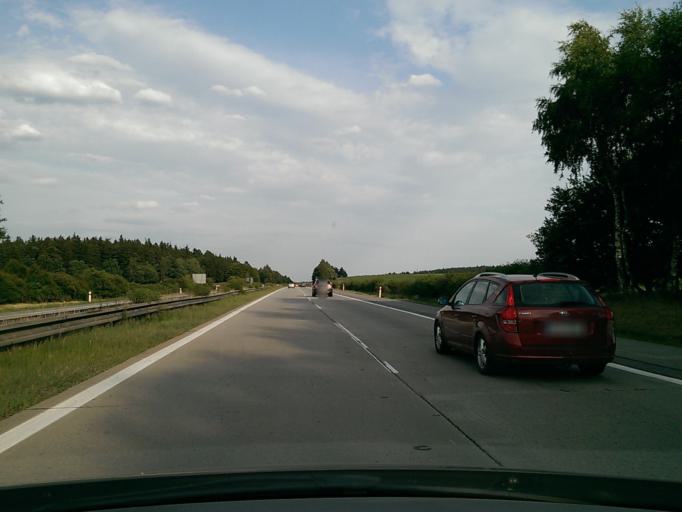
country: CZ
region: Vysocina
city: Dobronin
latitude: 49.4405
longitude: 15.6353
